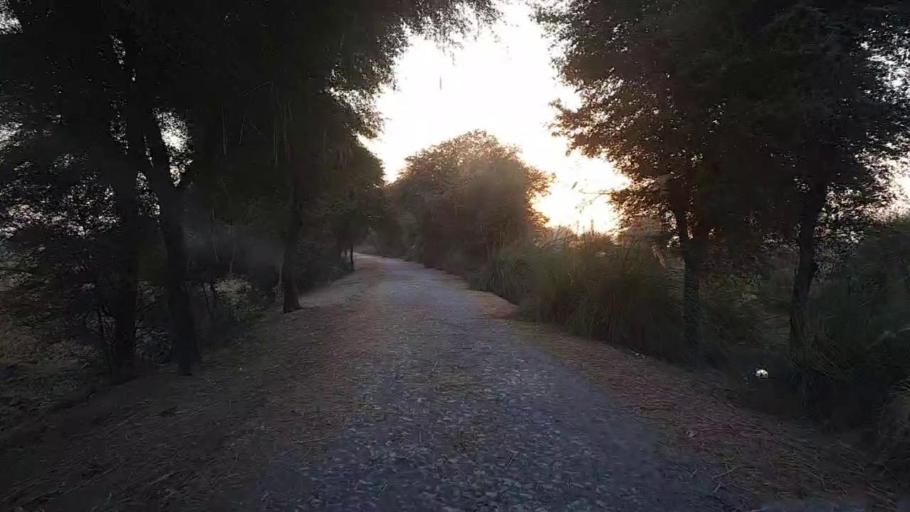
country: PK
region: Sindh
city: Kashmor
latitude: 28.4151
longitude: 69.4481
